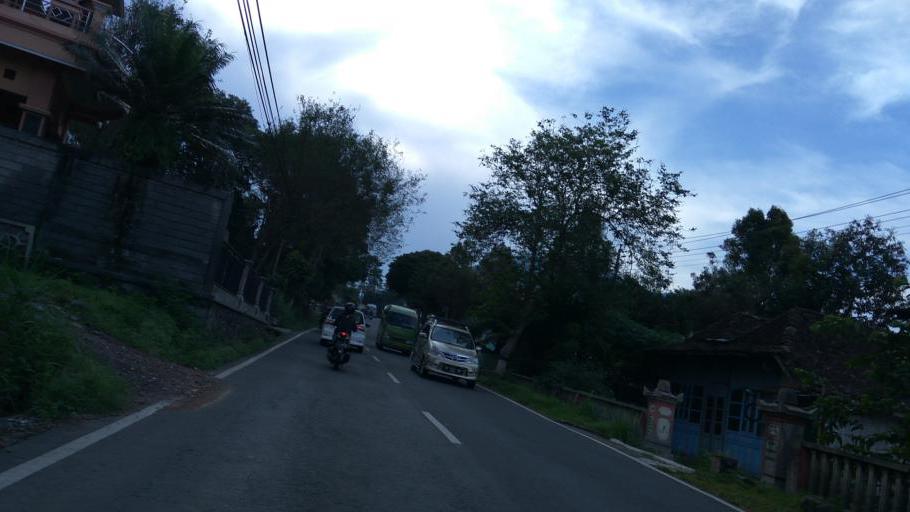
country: ID
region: Central Java
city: Gunung Kendil
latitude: -7.3763
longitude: 110.4329
